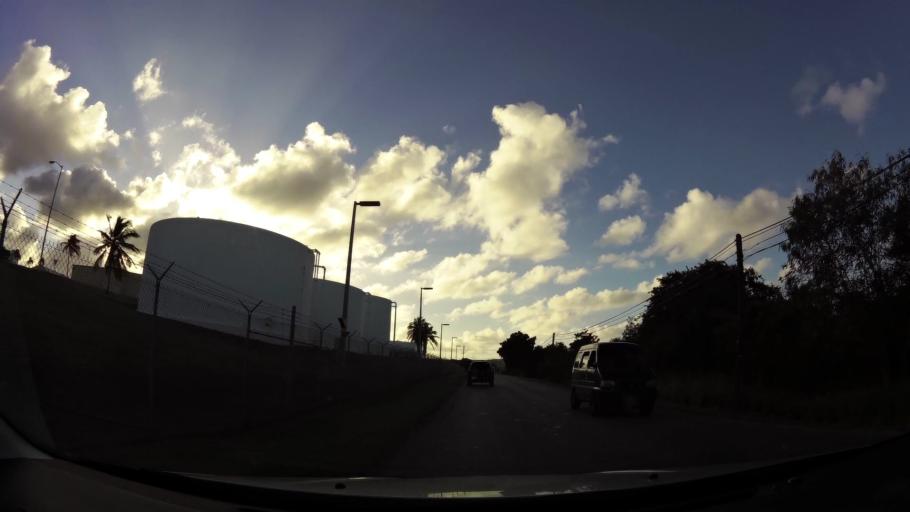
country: AG
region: Saint George
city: Piggotts
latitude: 17.1514
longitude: -61.7925
